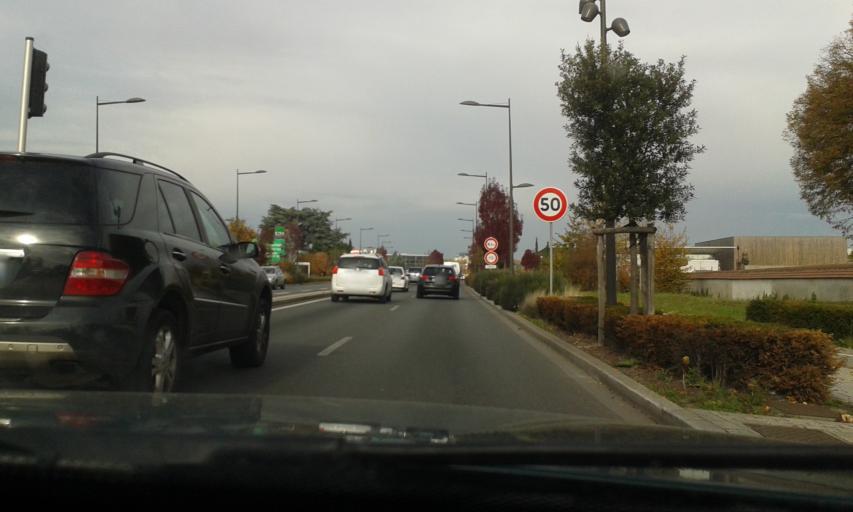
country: FR
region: Centre
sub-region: Departement du Loiret
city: Orleans
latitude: 47.8855
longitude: 1.8972
